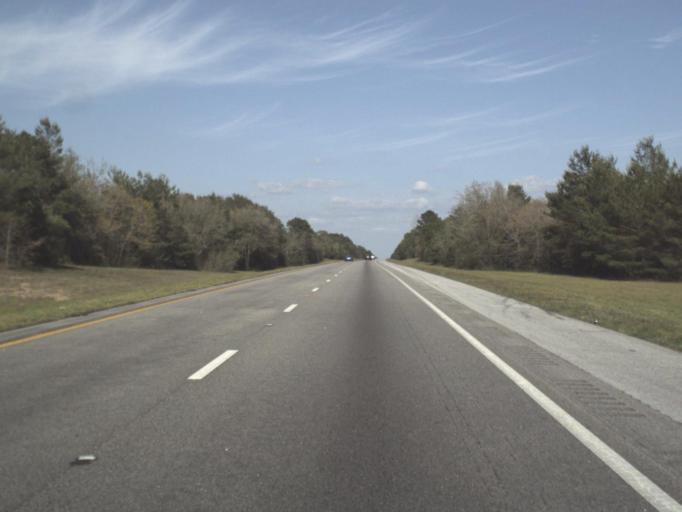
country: US
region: Florida
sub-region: Okaloosa County
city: Crestview
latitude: 30.7205
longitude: -86.4236
